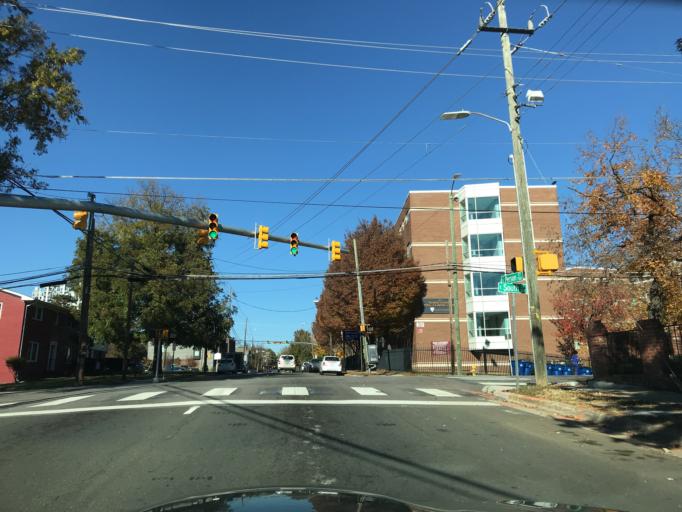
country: US
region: North Carolina
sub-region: Wake County
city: Raleigh
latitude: 35.7716
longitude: -78.6353
